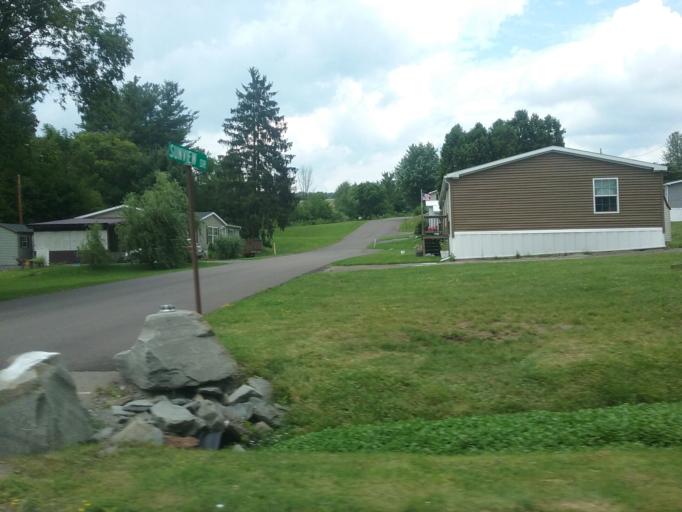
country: US
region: Pennsylvania
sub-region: Tioga County
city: Wellsboro
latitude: 41.7436
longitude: -77.2656
